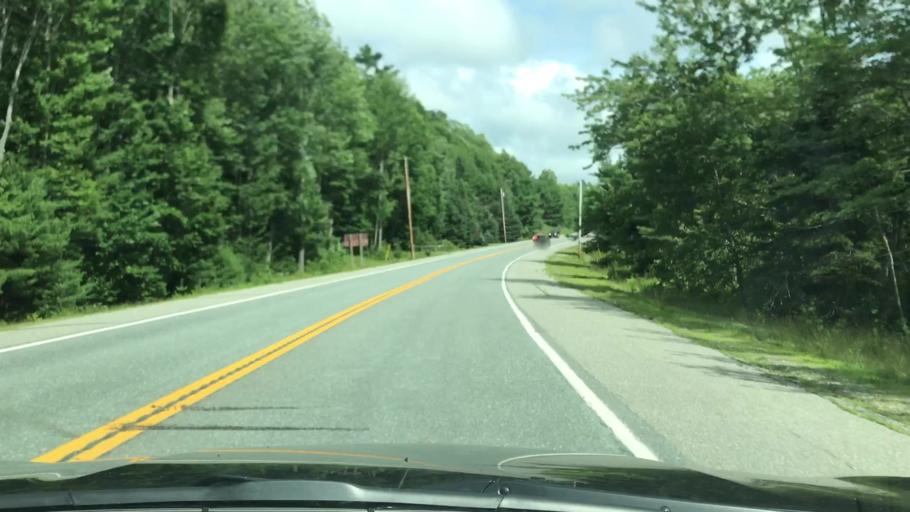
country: US
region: Maine
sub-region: Hancock County
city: Orland
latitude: 44.5675
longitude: -68.6748
